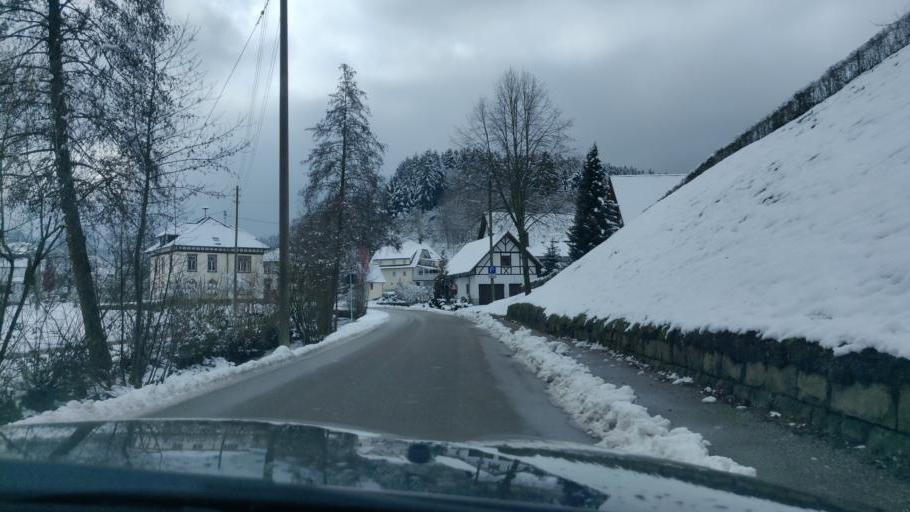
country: DE
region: Baden-Wuerttemberg
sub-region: Freiburg Region
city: Lautenbach
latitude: 48.5021
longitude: 8.0886
